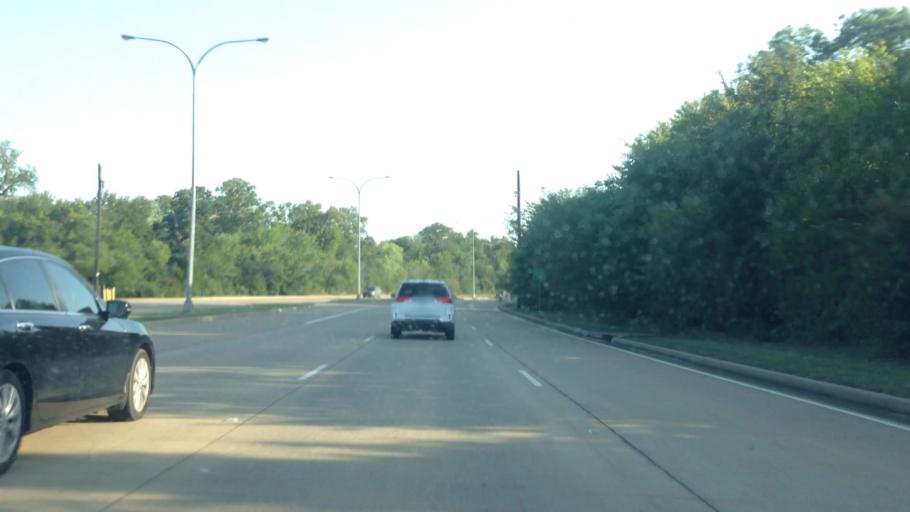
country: US
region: Texas
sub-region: Tarrant County
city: Pantego
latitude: 32.7420
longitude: -97.1735
